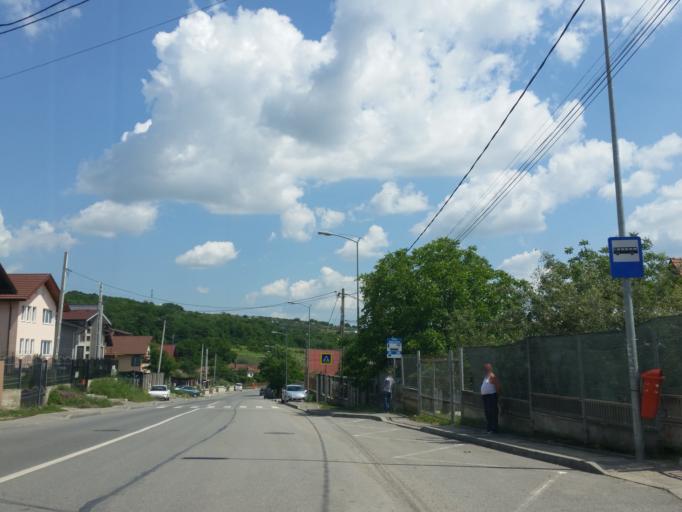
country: RO
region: Cluj
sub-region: Municipiul Cluj-Napoca
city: Cluj-Napoca
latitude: 46.8208
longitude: 23.5953
